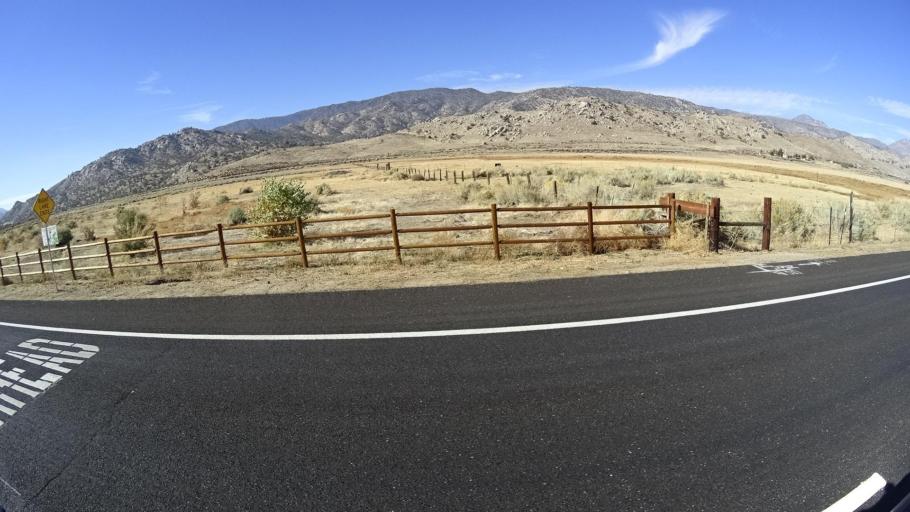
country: US
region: California
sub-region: Kern County
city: Lake Isabella
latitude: 35.6177
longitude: -118.4770
